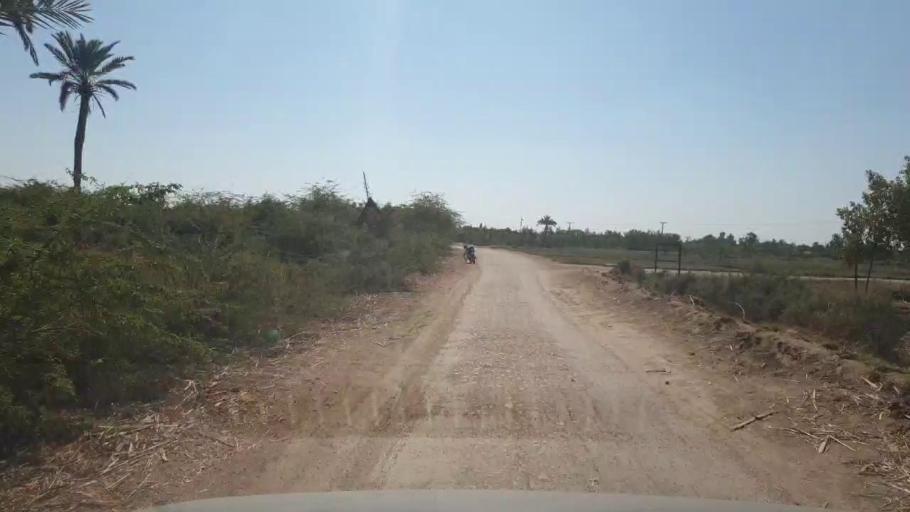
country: PK
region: Sindh
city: Mirwah Gorchani
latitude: 25.3007
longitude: 69.1310
